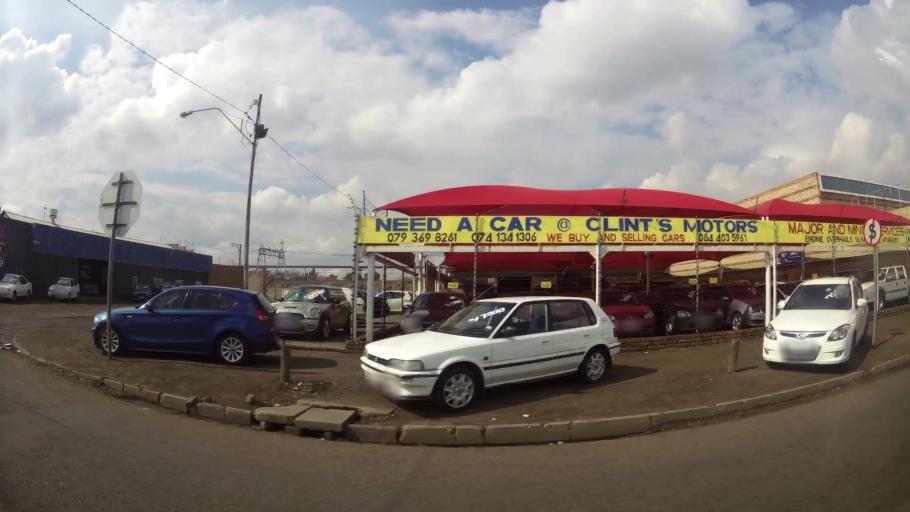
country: ZA
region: Gauteng
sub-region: Sedibeng District Municipality
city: Vereeniging
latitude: -26.6823
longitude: 27.9322
